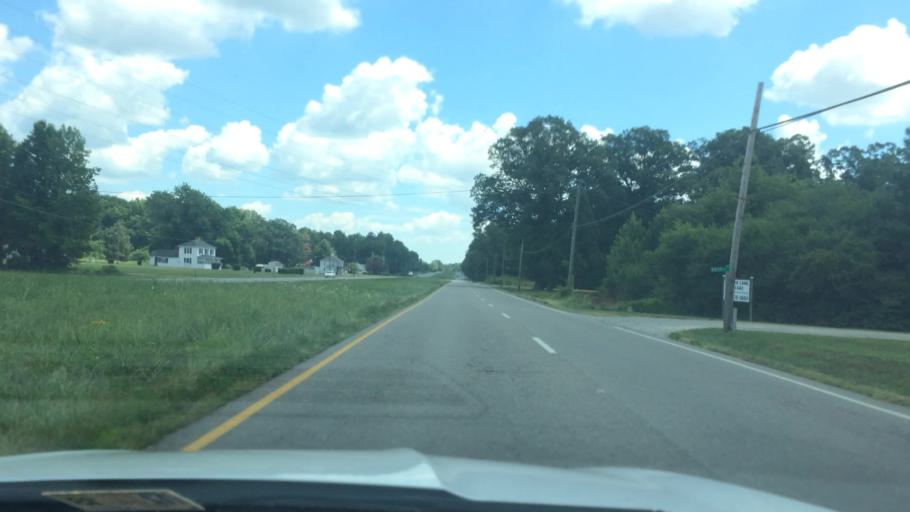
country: US
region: Virginia
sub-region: King William County
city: West Point
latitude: 37.5434
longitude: -76.7483
